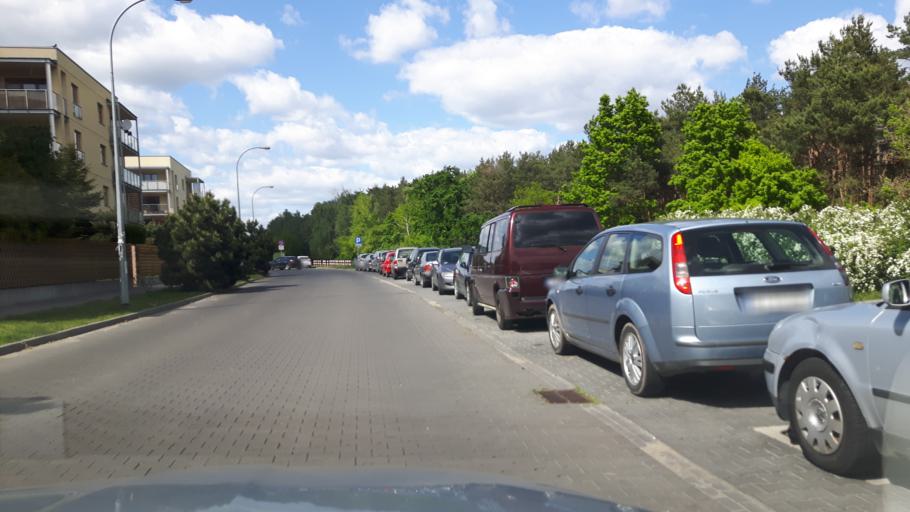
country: PL
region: Masovian Voivodeship
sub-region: Warszawa
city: Targowek
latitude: 52.2930
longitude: 21.0574
